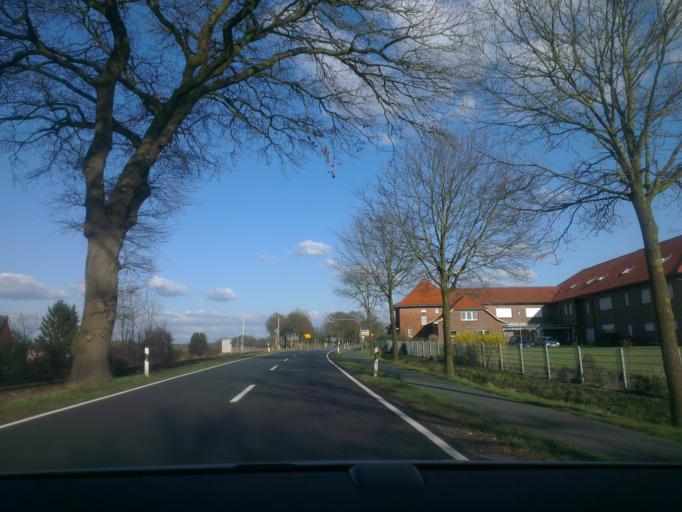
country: DE
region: Lower Saxony
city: Lastrup
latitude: 52.7367
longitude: 7.8607
